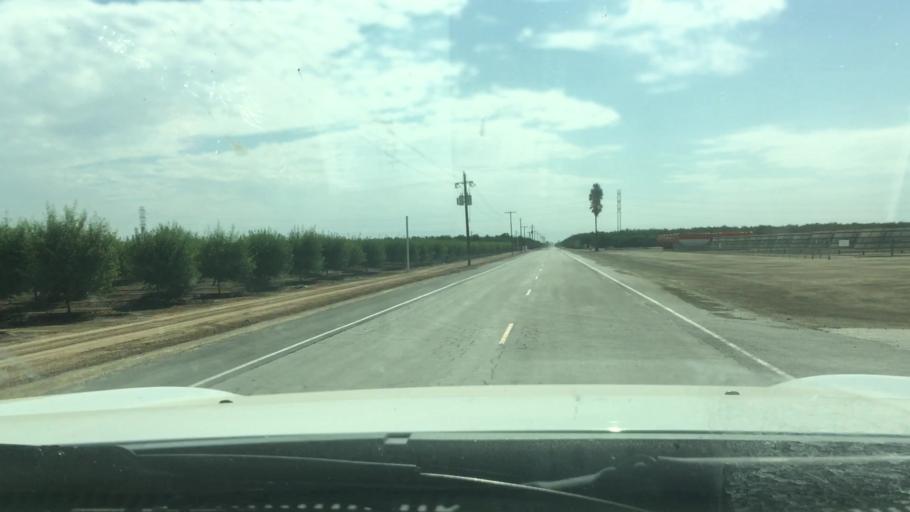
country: US
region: California
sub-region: Kern County
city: Wasco
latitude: 35.5577
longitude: -119.4518
